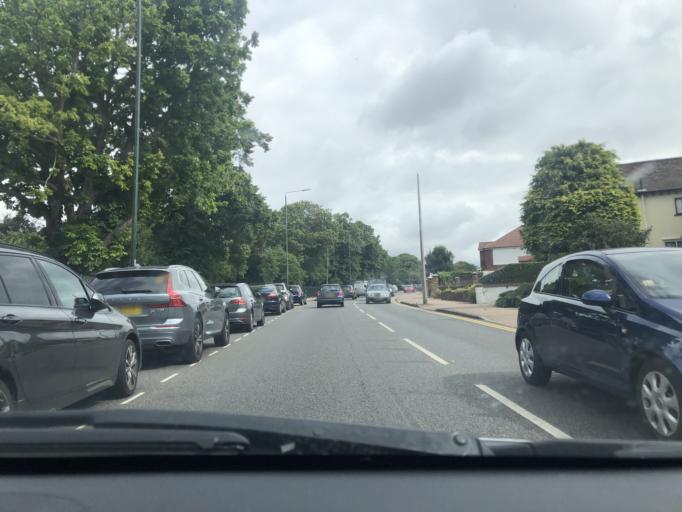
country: GB
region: England
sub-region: Greater London
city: Welling
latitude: 51.4539
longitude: 0.1228
